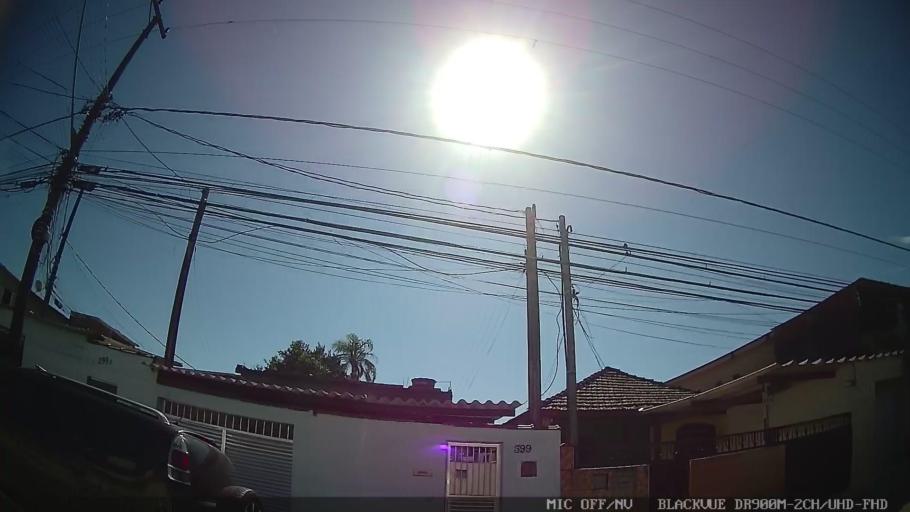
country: BR
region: Sao Paulo
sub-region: Santos
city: Santos
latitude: -23.9546
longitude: -46.2928
